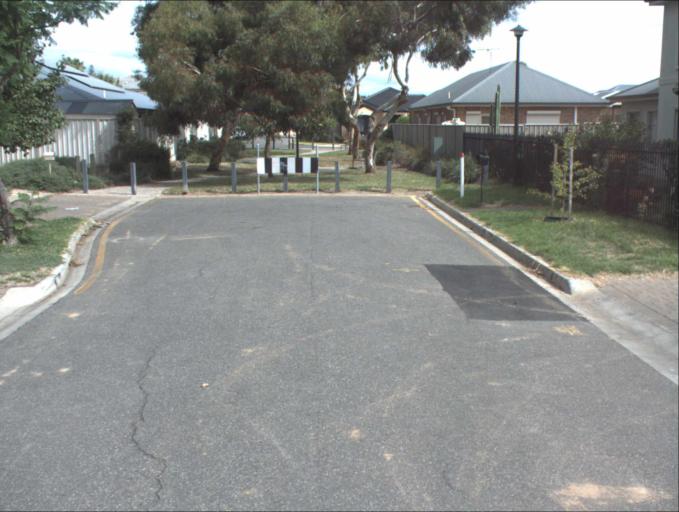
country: AU
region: South Australia
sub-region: Port Adelaide Enfield
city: Blair Athol
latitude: -34.8675
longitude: 138.5917
